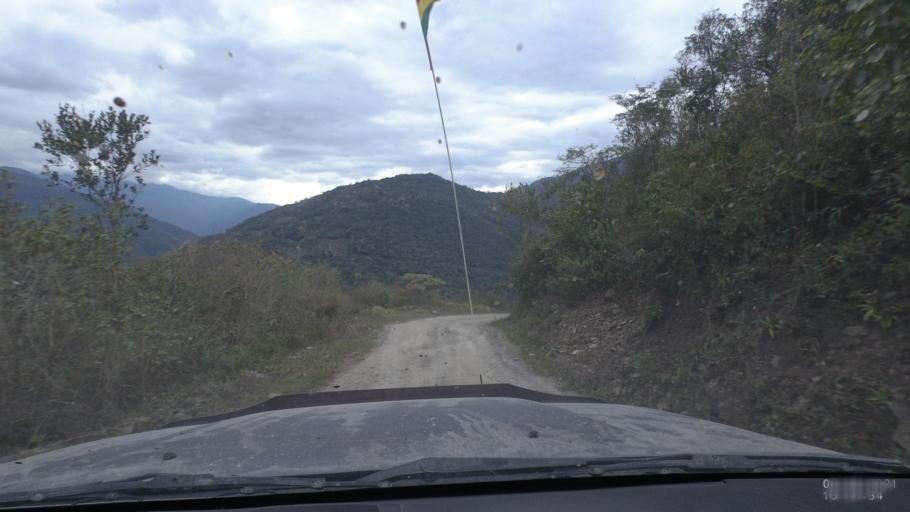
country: BO
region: La Paz
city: Quime
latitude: -16.5378
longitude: -66.7610
